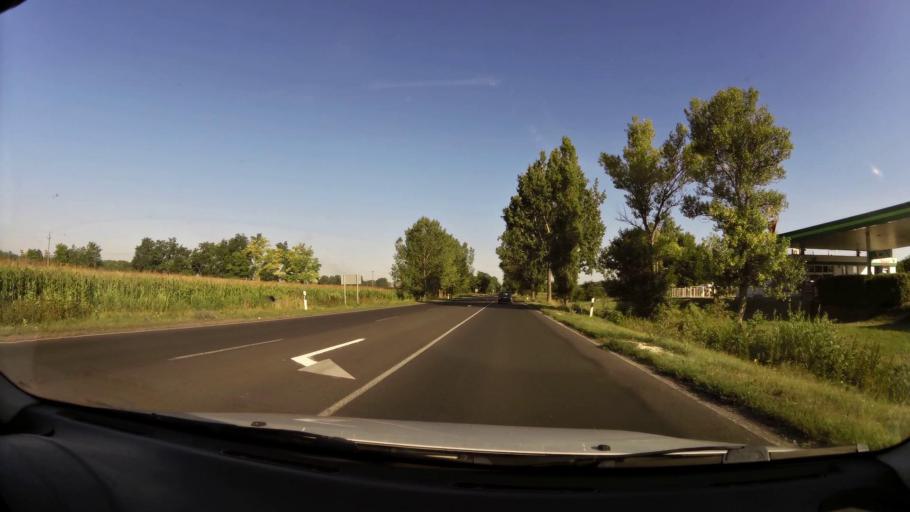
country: HU
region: Pest
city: Monor
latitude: 47.3192
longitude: 19.4756
